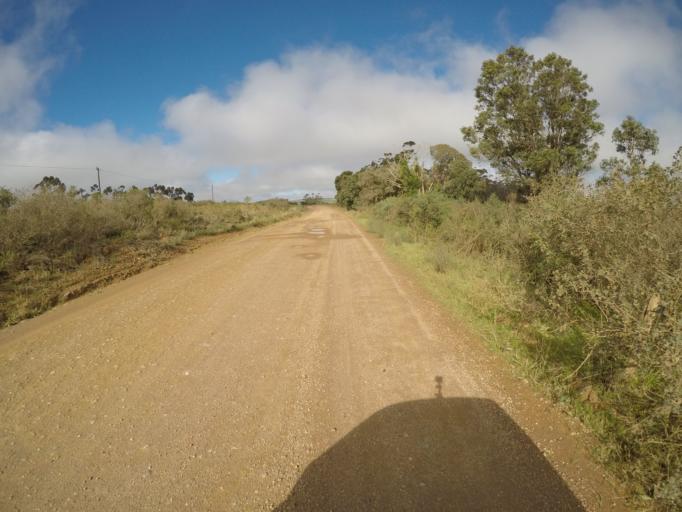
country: ZA
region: Western Cape
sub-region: Cape Winelands District Municipality
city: Ashton
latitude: -34.1207
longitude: 19.8070
